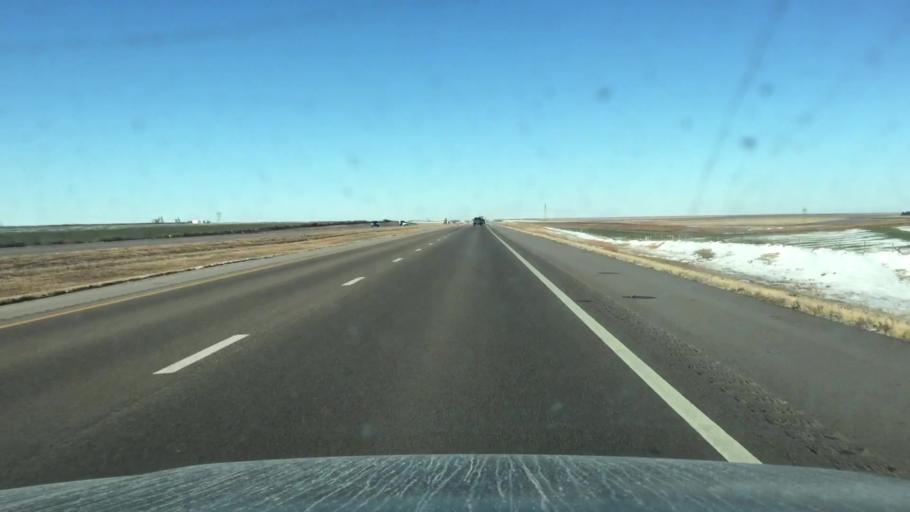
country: US
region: Kansas
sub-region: Logan County
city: Oakley
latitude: 39.2528
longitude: -100.9206
